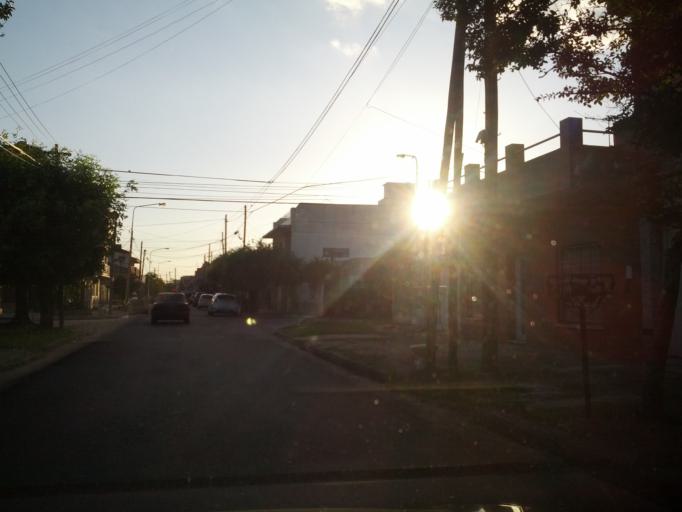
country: AR
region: Buenos Aires
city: San Justo
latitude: -34.6572
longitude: -58.5443
